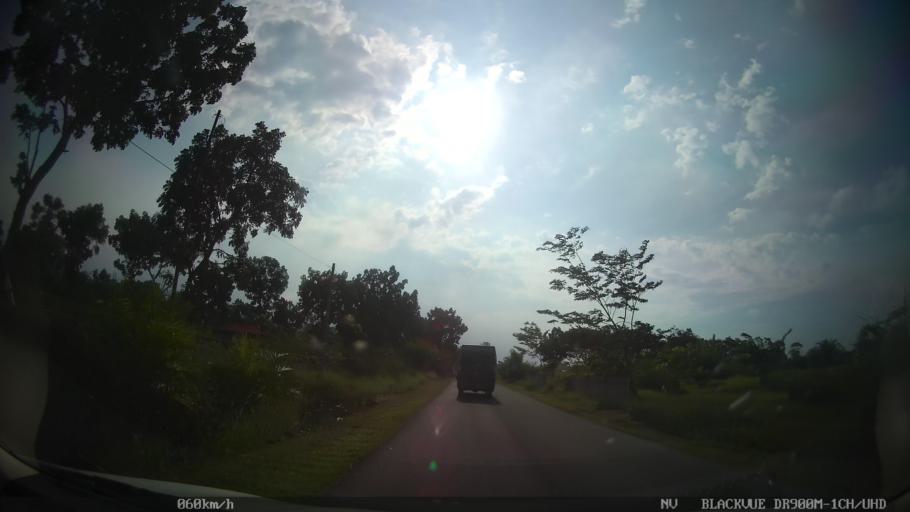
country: ID
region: North Sumatra
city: Percut
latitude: 3.5933
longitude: 98.7990
